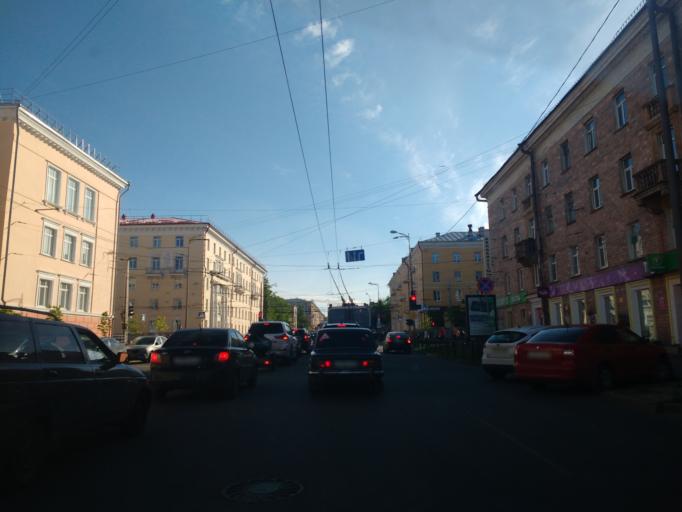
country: RU
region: Republic of Karelia
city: Petrozavodsk
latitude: 61.7877
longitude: 34.3557
